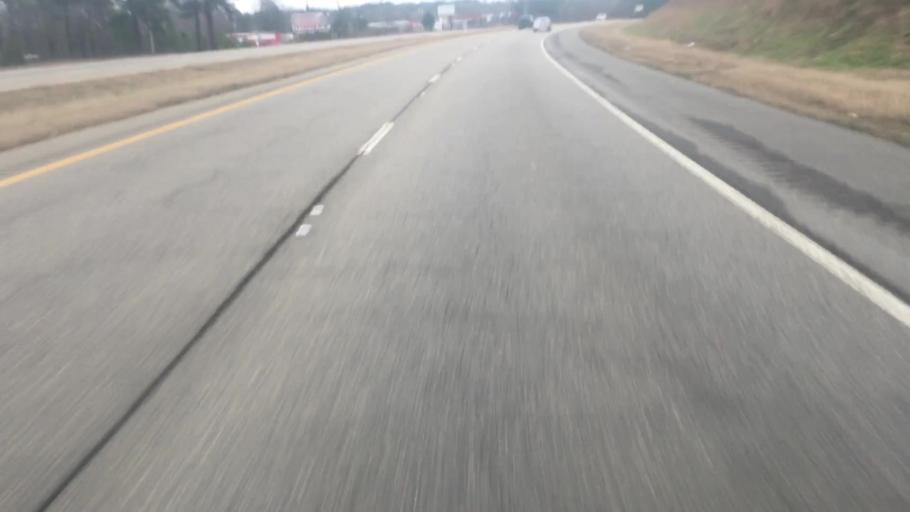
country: US
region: Alabama
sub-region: Walker County
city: Cordova
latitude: 33.8211
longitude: -87.1564
